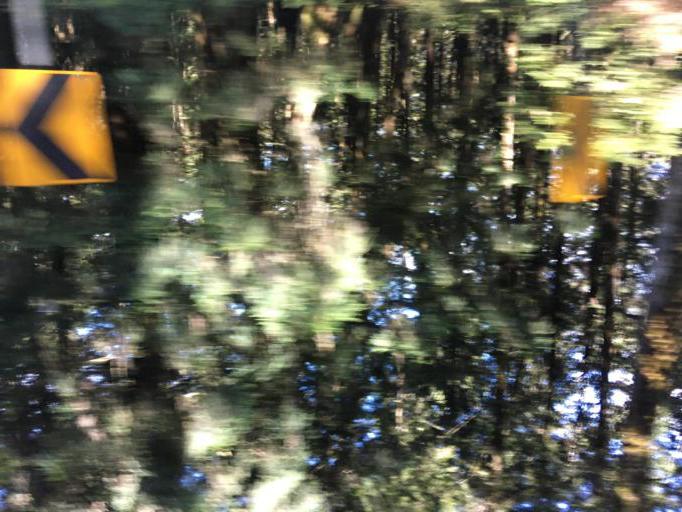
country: TW
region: Taiwan
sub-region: Yilan
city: Yilan
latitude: 24.5153
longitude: 121.5216
